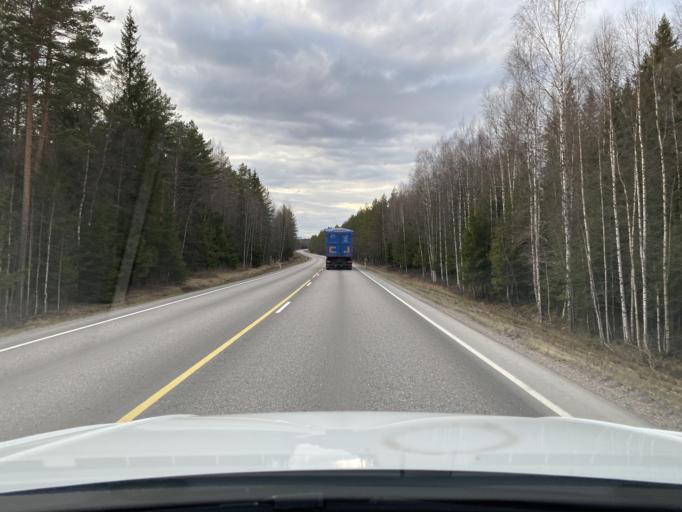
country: FI
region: Uusimaa
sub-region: Helsinki
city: Kaerkoelae
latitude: 60.8077
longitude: 24.0654
